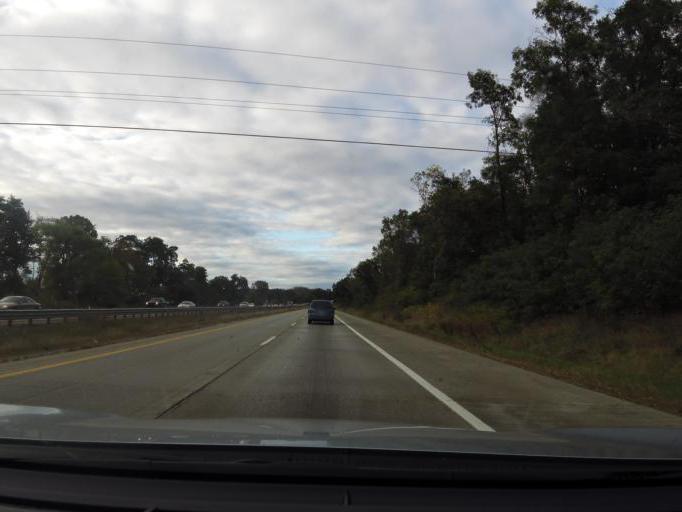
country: US
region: Michigan
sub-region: Livingston County
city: Brighton
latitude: 42.6559
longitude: -83.7576
